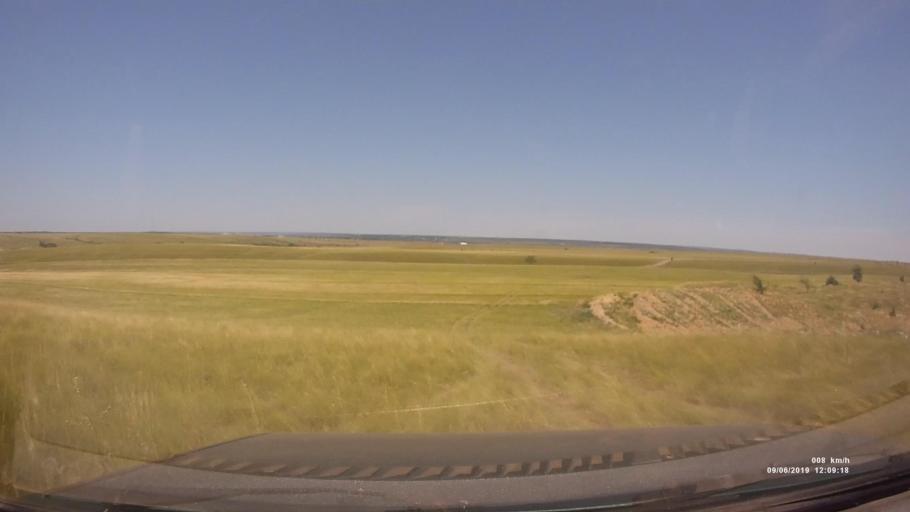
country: RU
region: Rostov
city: Staraya Stanitsa
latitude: 48.2477
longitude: 40.3380
